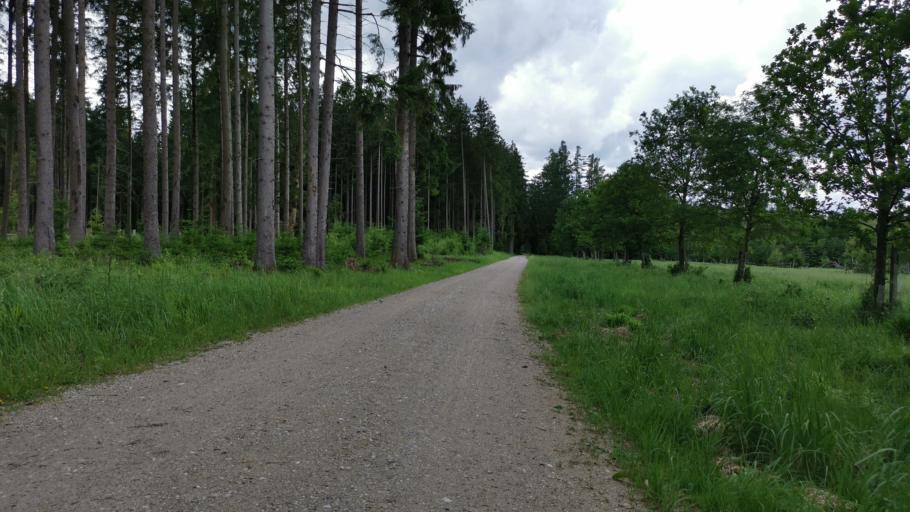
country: DE
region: Bavaria
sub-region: Upper Bavaria
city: Baierbrunn
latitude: 48.0473
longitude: 11.4893
